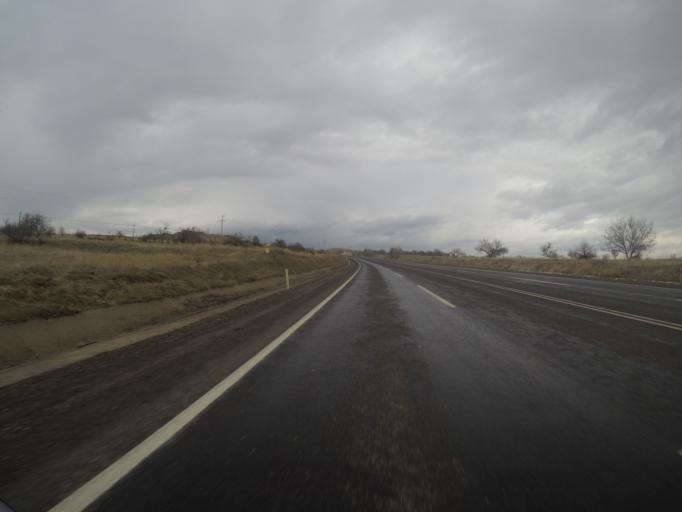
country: TR
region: Nevsehir
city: Urgub
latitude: 38.6352
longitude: 34.8746
